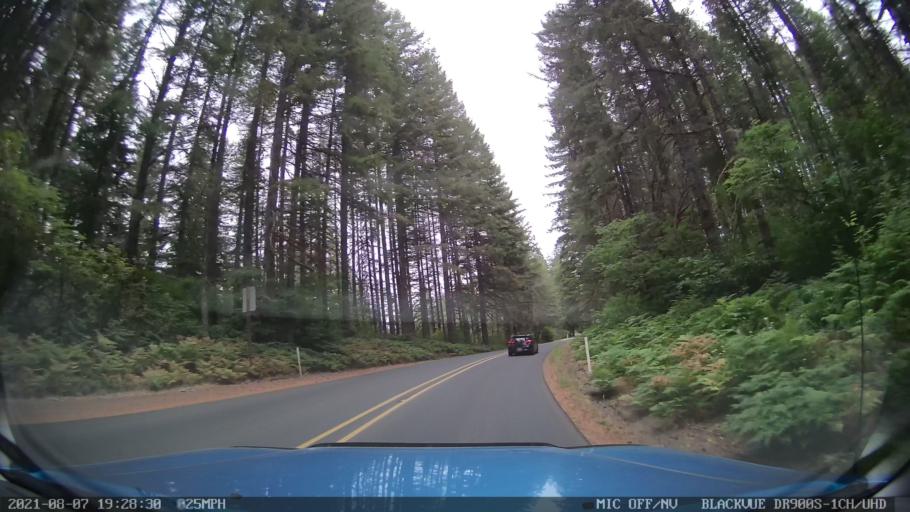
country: US
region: Oregon
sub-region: Linn County
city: Lyons
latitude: 44.8847
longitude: -122.6390
